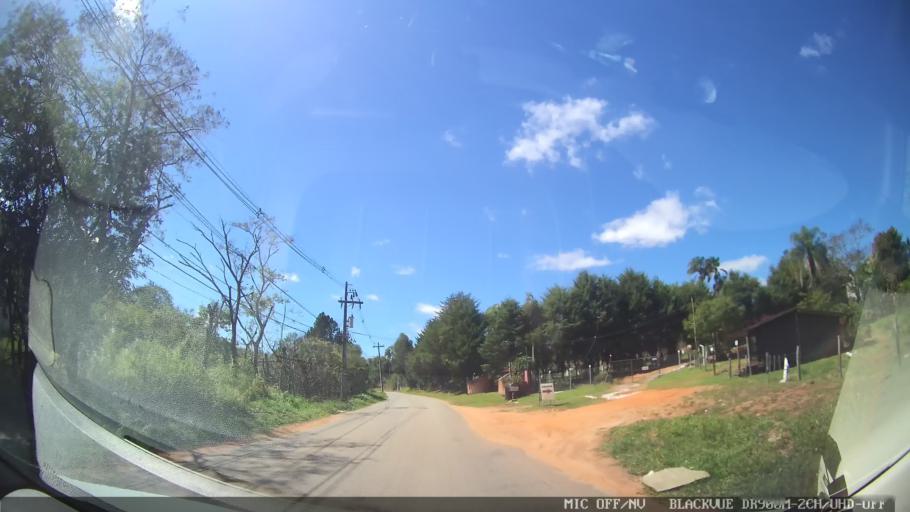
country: BR
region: Sao Paulo
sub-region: Jarinu
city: Jarinu
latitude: -23.1623
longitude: -46.7328
